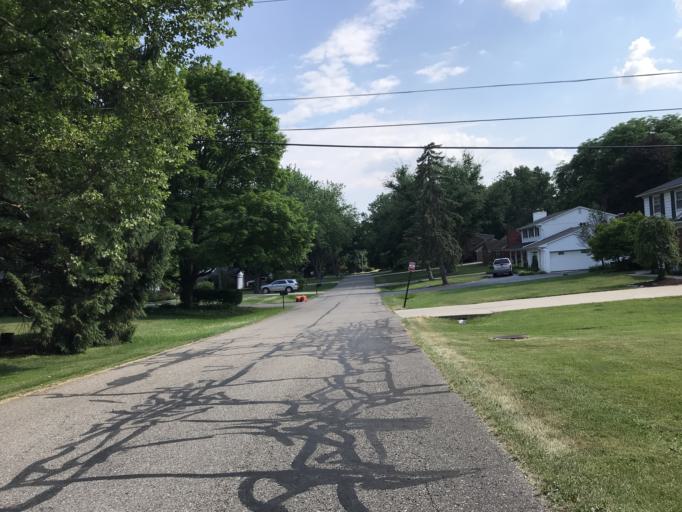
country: US
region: Michigan
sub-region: Oakland County
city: Farmington
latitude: 42.4654
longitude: -83.3890
